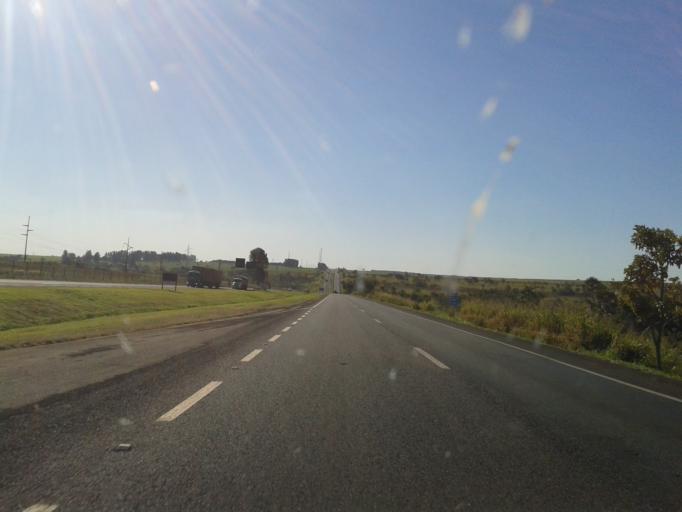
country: BR
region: Minas Gerais
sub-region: Uberlandia
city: Uberlandia
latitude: -19.1648
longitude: -48.1621
